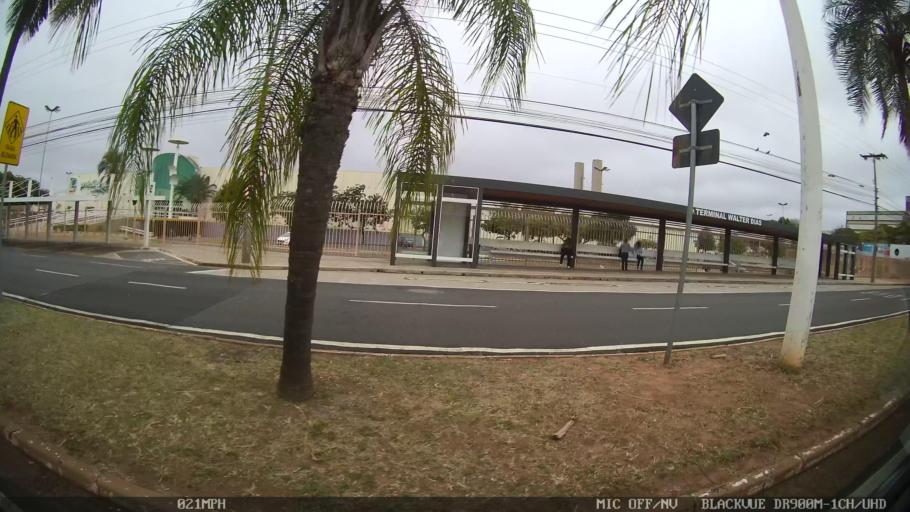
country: BR
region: Sao Paulo
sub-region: Sao Jose Do Rio Preto
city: Sao Jose do Rio Preto
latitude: -20.8358
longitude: -49.4004
